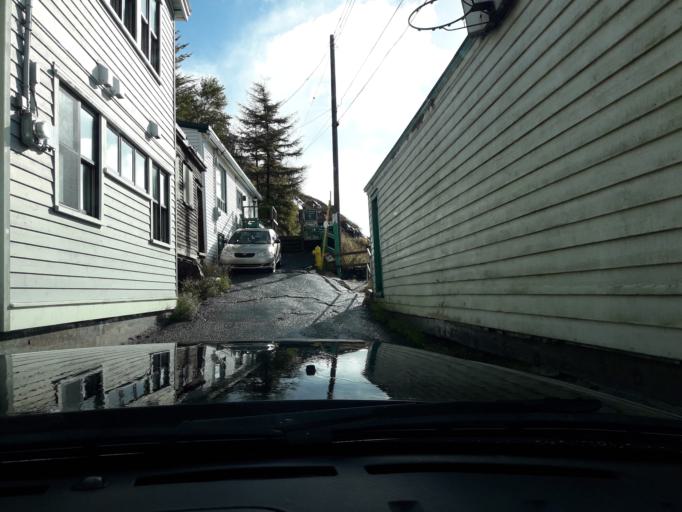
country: CA
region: Newfoundland and Labrador
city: St. John's
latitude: 47.5681
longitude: -52.6883
